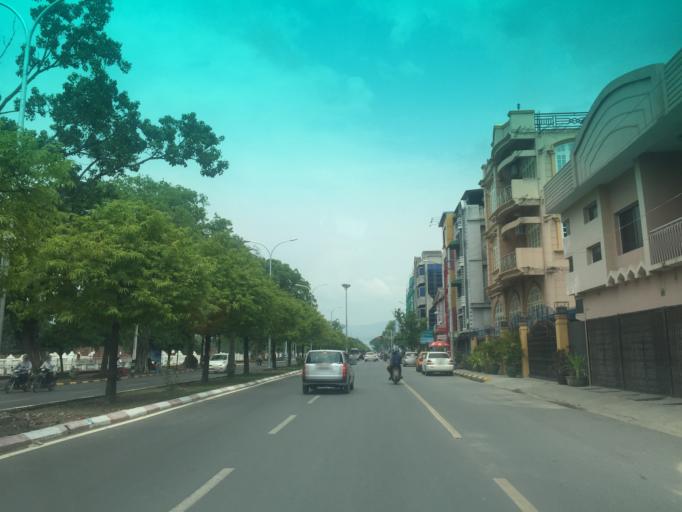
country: MM
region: Mandalay
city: Mandalay
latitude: 21.9825
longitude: 96.0945
